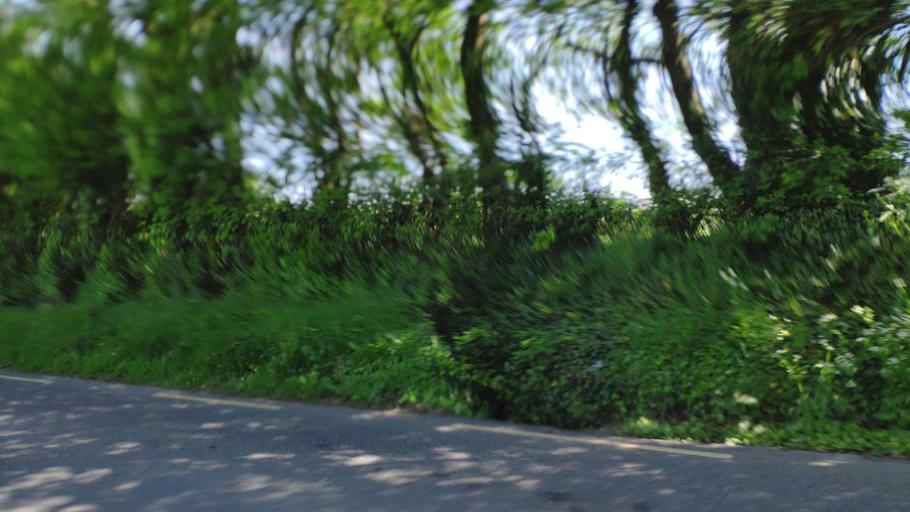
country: IE
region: Munster
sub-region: County Cork
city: Blarney
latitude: 51.9250
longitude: -8.5553
